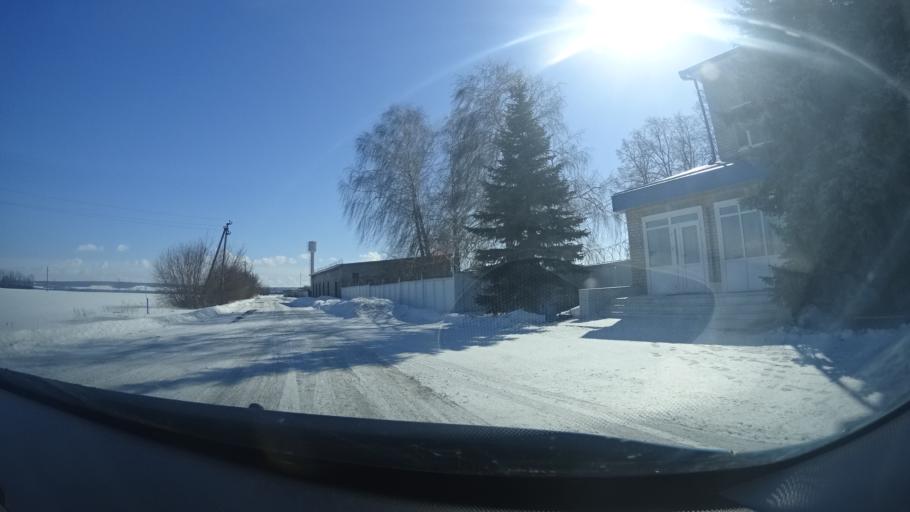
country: RU
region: Bashkortostan
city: Chishmy
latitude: 54.5887
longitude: 55.4078
